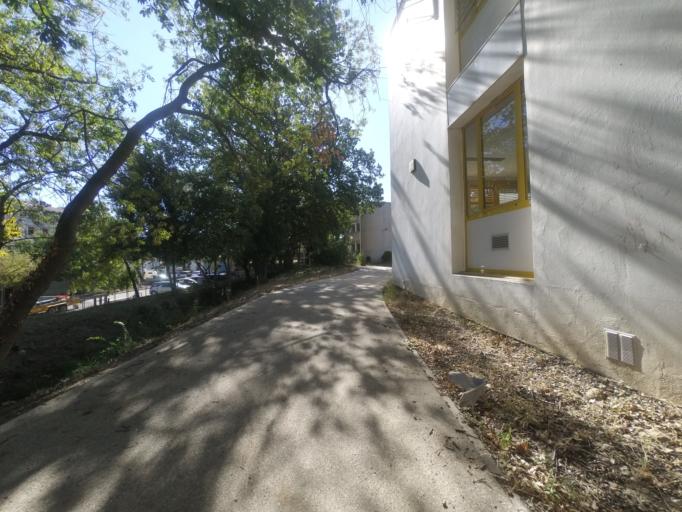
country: FR
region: Languedoc-Roussillon
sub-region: Departement des Pyrenees-Orientales
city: Perpignan
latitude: 42.6830
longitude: 2.8983
